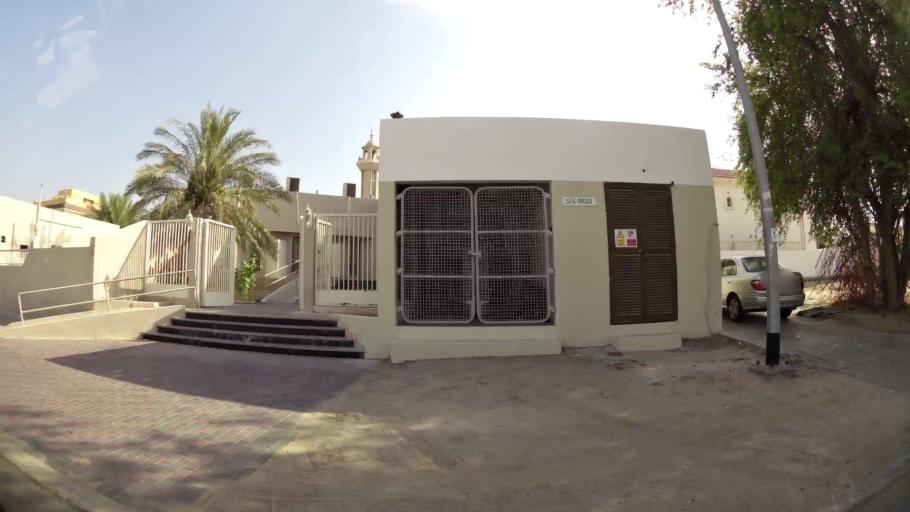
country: AE
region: Ash Shariqah
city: Sharjah
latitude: 25.2233
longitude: 55.3953
